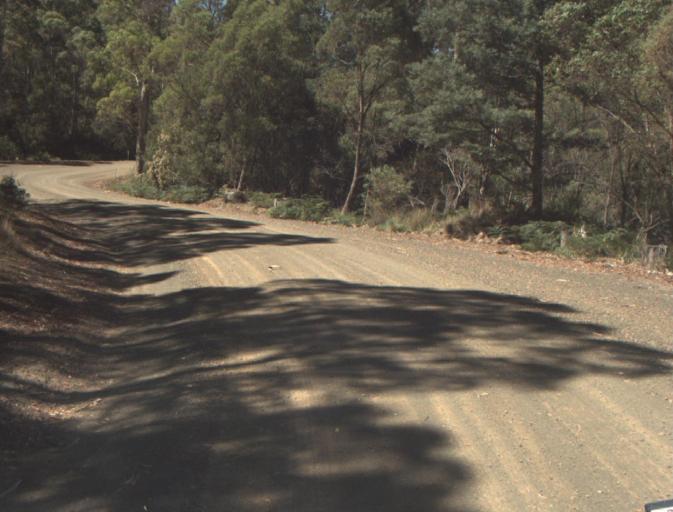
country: AU
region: Tasmania
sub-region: Launceston
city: Newstead
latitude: -41.3073
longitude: 147.3347
